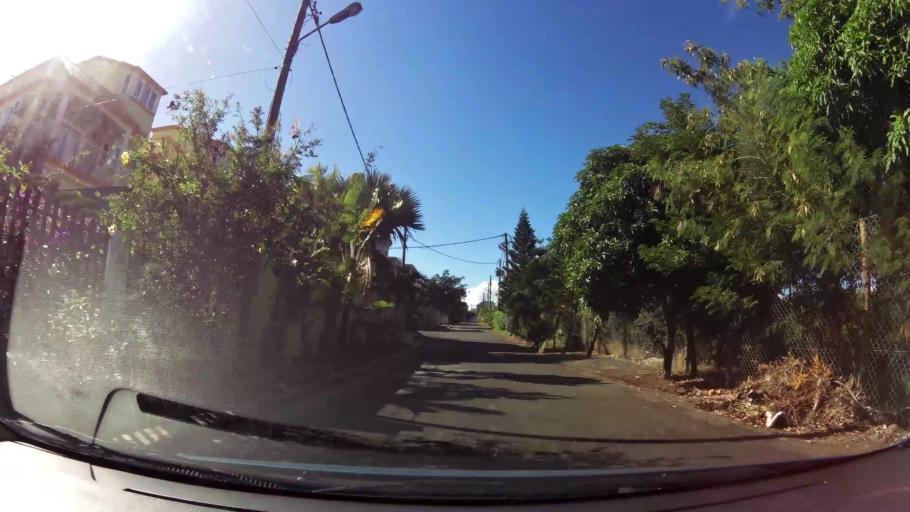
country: MU
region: Black River
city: Flic en Flac
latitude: -20.2803
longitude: 57.3781
